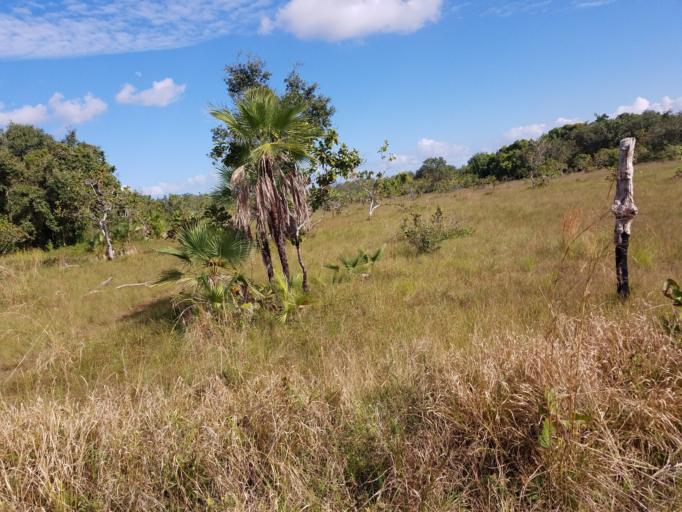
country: BZ
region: Belize
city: Belize City
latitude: 17.5642
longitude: -88.4116
